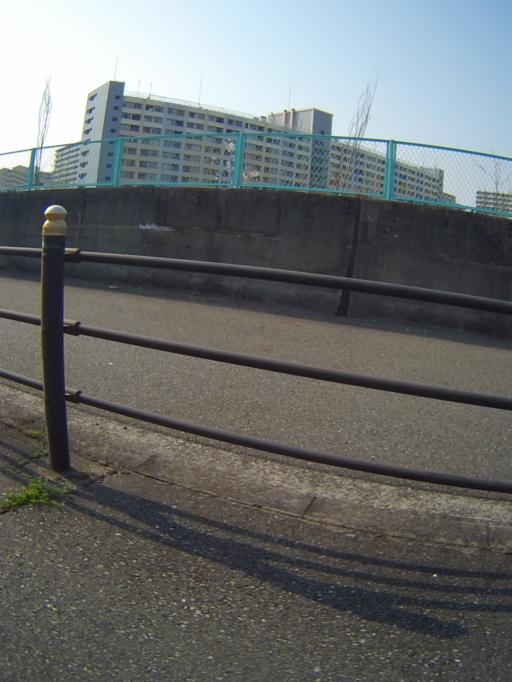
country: JP
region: Osaka
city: Osaka-shi
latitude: 34.6868
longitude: 135.4616
